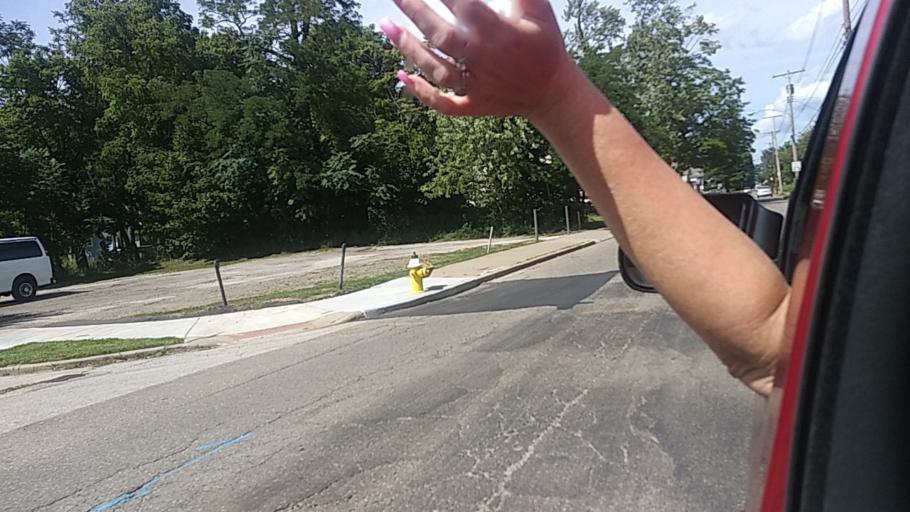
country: US
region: Ohio
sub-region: Summit County
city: Akron
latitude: 41.0870
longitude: -81.5500
